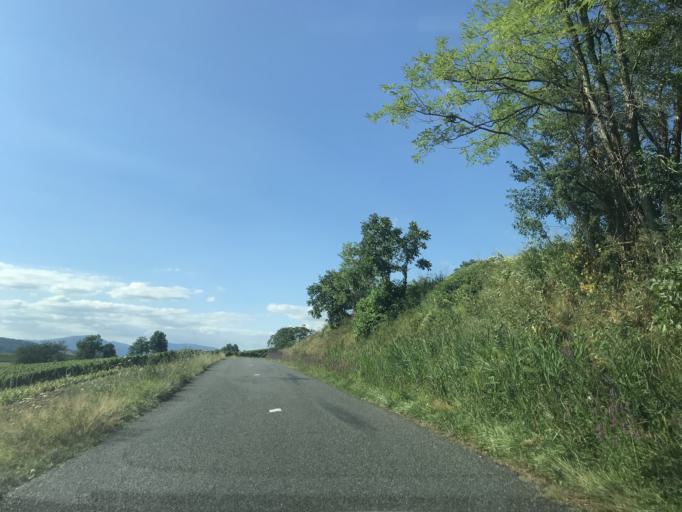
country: FR
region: Rhone-Alpes
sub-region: Departement de la Savoie
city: Yenne
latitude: 45.7227
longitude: 5.8040
